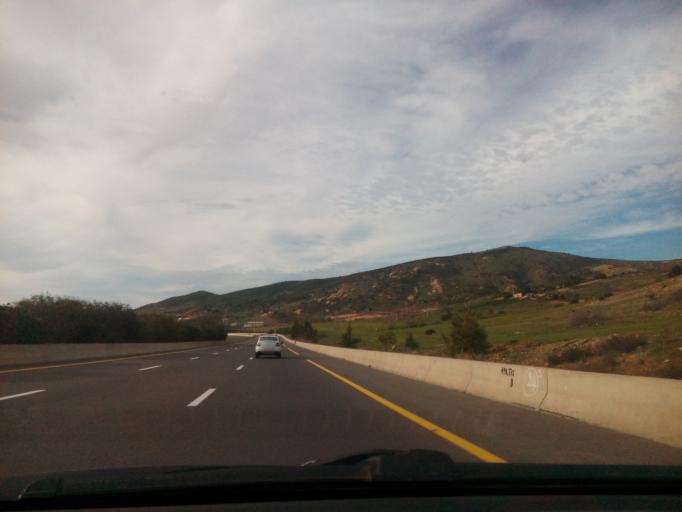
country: DZ
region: Sidi Bel Abbes
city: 'Ain el Berd
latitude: 35.3868
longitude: -0.4932
